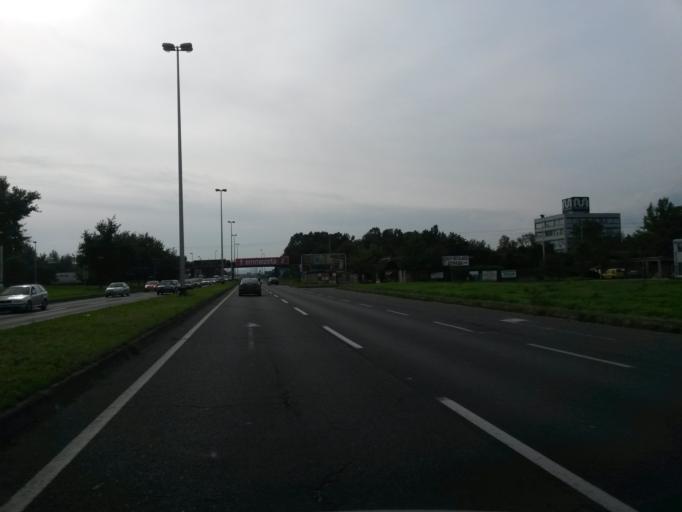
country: HR
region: Grad Zagreb
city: Dubrava
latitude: 45.8024
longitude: 16.0652
